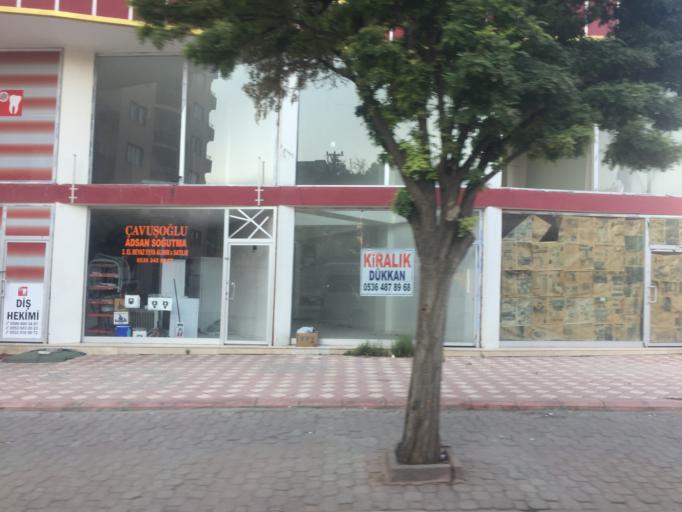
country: TR
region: Mardin
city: Midyat
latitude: 37.4293
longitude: 41.3384
